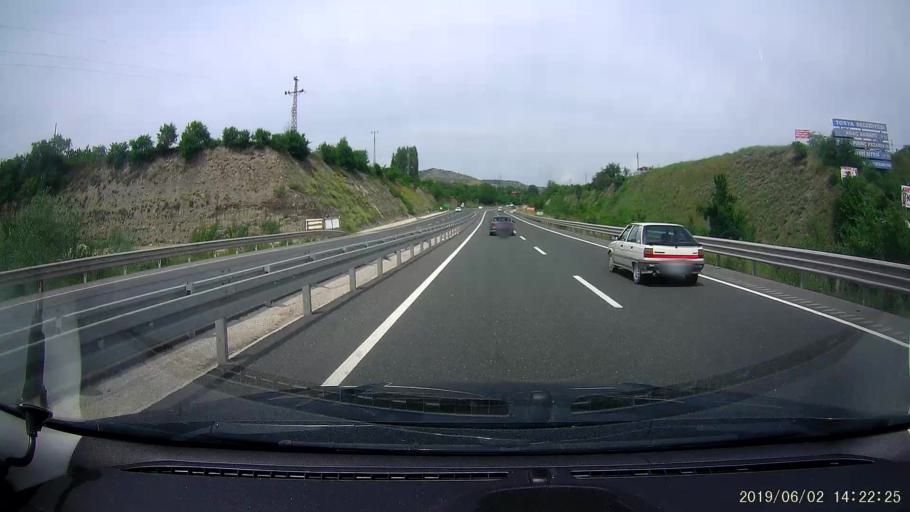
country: TR
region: Kastamonu
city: Tosya
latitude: 40.9933
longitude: 34.0164
